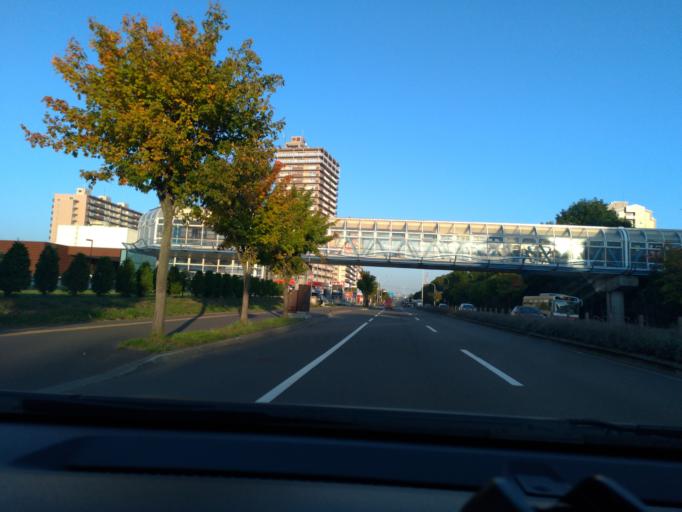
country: JP
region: Hokkaido
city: Ishikari
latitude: 43.1582
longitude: 141.3987
